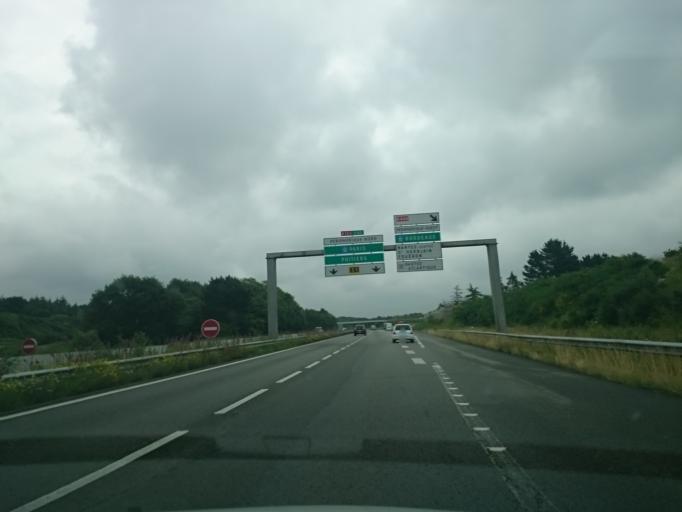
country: FR
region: Pays de la Loire
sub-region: Departement de la Loire-Atlantique
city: Sautron
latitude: 47.2562
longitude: -1.6869
